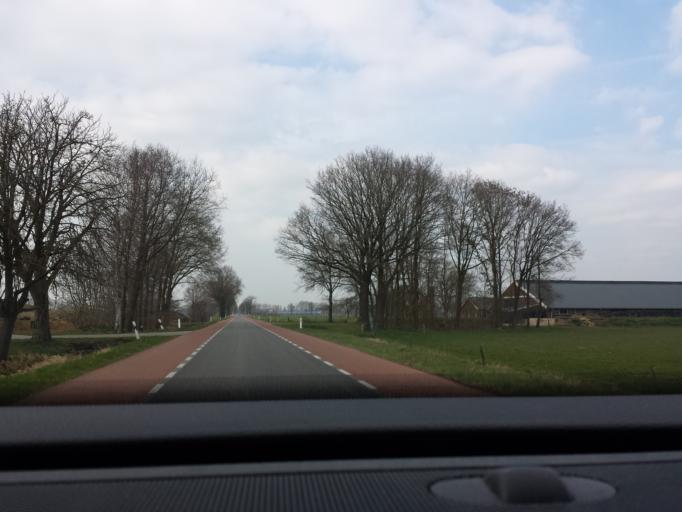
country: NL
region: Gelderland
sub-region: Oost Gelre
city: Lichtenvoorde
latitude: 52.0295
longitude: 6.4899
